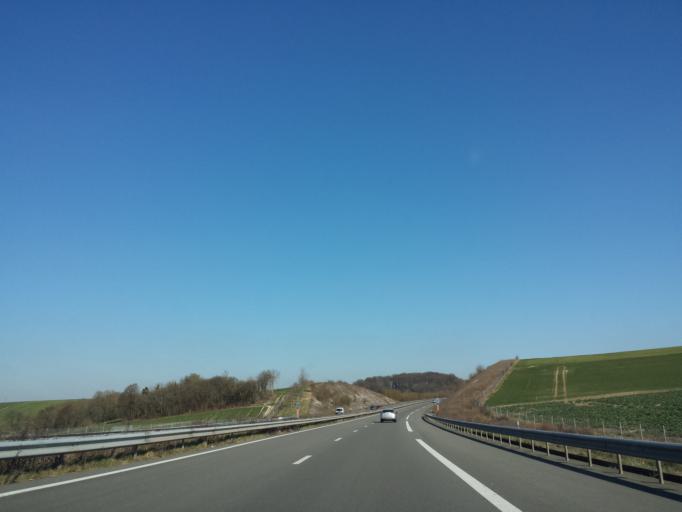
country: FR
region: Picardie
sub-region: Departement de la Somme
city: Conty
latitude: 49.6733
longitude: 2.2098
